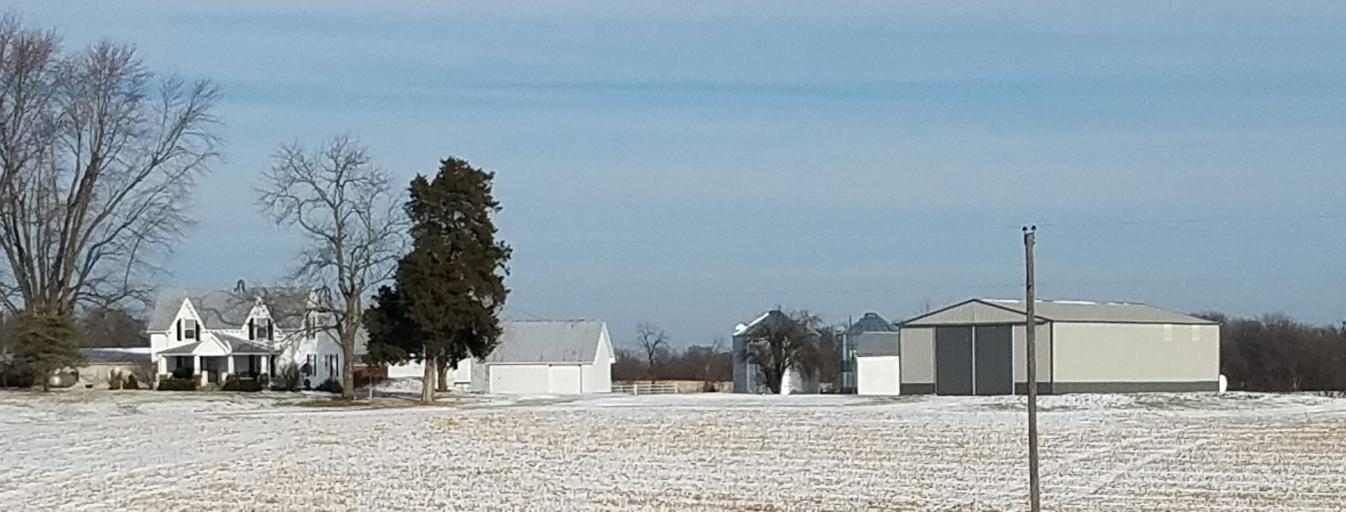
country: US
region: Missouri
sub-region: Jackson County
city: Oak Grove
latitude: 39.0912
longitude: -94.1173
